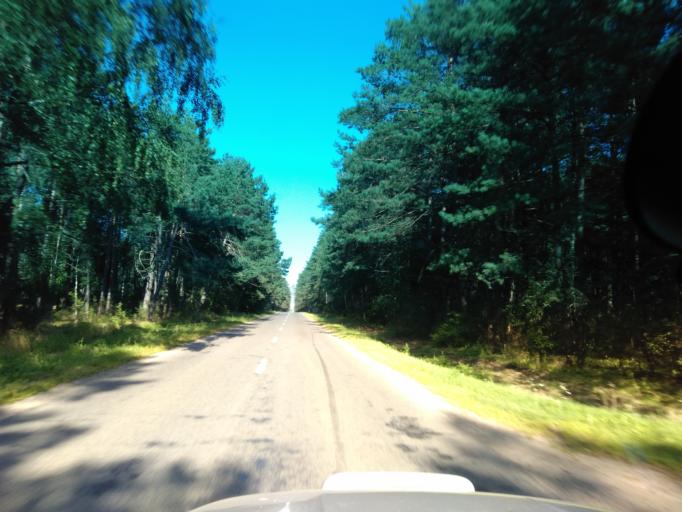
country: BY
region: Minsk
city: Uzda
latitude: 53.4596
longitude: 27.1698
